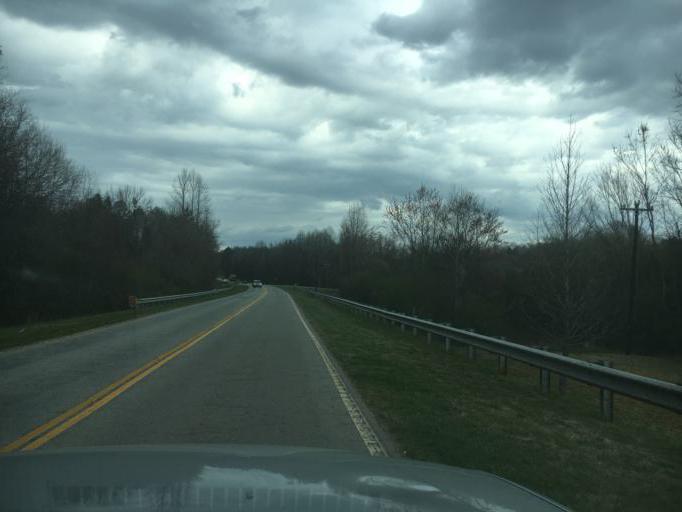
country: US
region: South Carolina
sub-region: Oconee County
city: Walhalla
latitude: 34.7417
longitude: -83.0503
